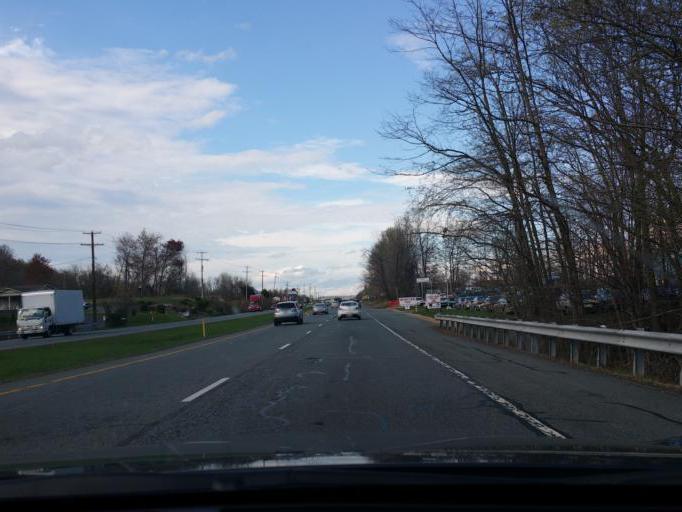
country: US
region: Maryland
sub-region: Harford County
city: Havre de Grace
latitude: 39.5410
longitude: -76.1103
